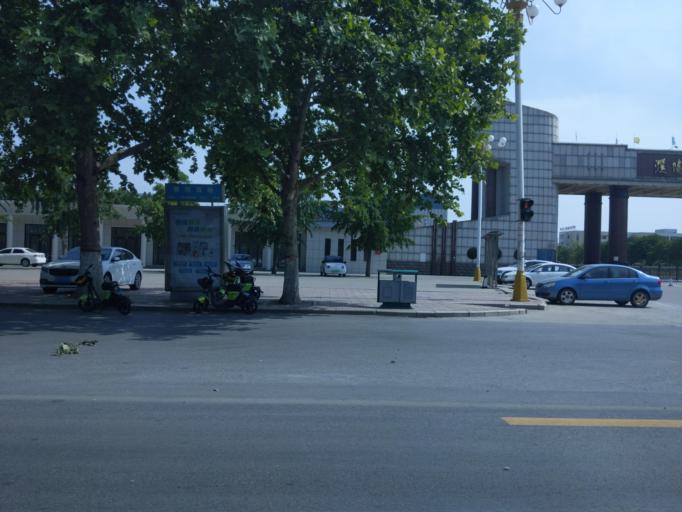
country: CN
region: Henan Sheng
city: Puyang
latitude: 35.7744
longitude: 114.9508
